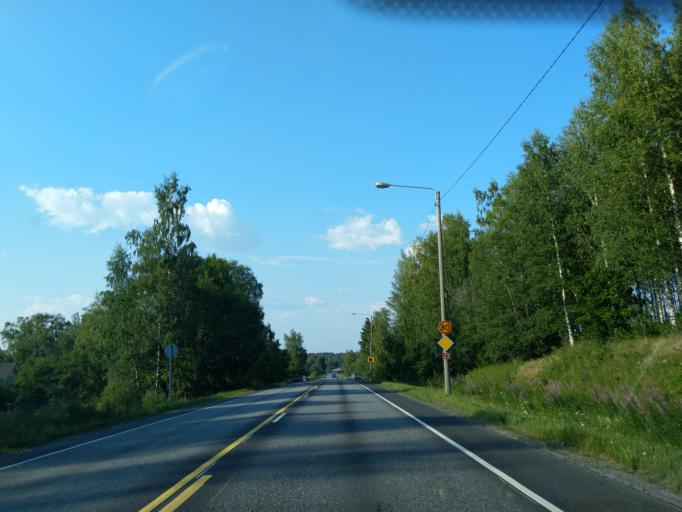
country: FI
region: Satakunta
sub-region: Pori
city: Pomarkku
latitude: 61.6914
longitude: 22.0004
